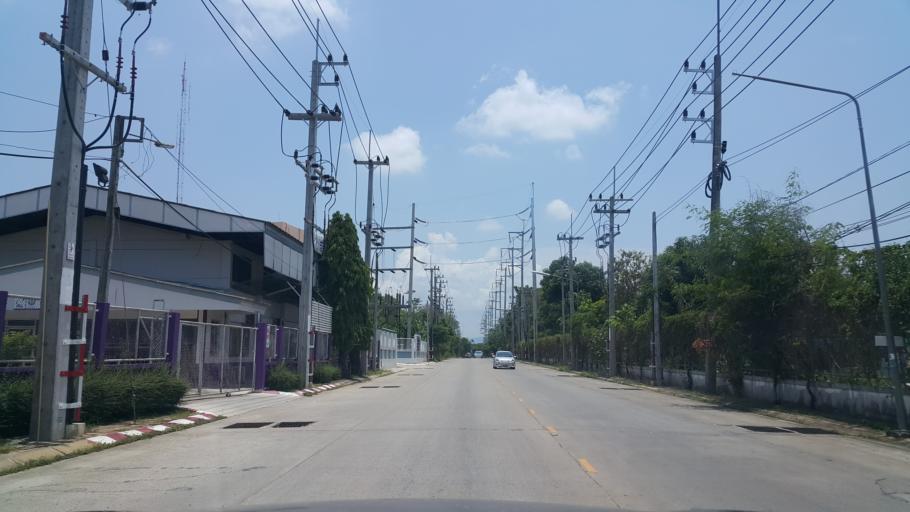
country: TH
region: Chiang Rai
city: Chiang Rai
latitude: 19.9120
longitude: 99.8219
